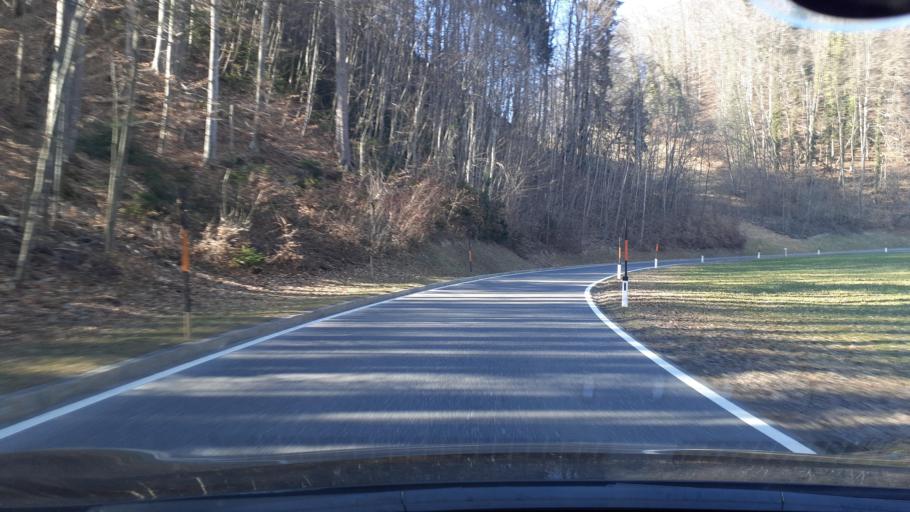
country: AT
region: Vorarlberg
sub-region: Politischer Bezirk Feldkirch
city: Fraxern
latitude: 47.3096
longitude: 9.6664
